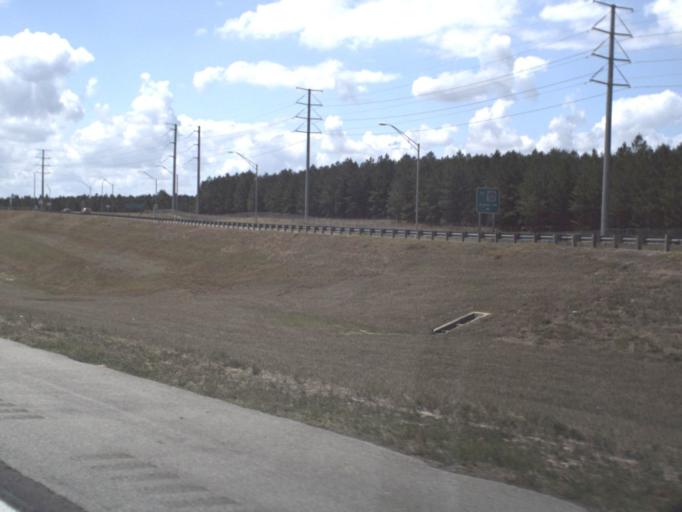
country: US
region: Florida
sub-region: Orange County
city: Oakland
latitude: 28.4774
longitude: -81.6318
